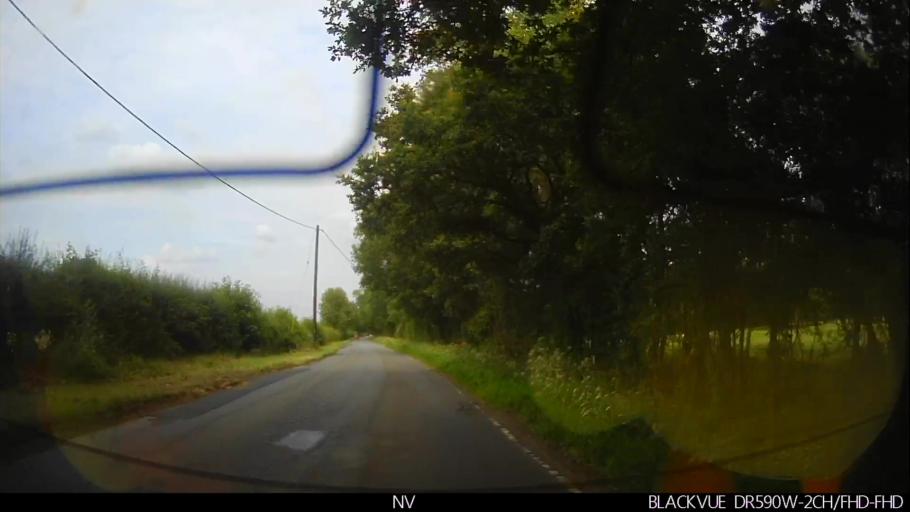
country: GB
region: England
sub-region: North Yorkshire
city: Strensall
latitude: 54.0380
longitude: -1.0201
